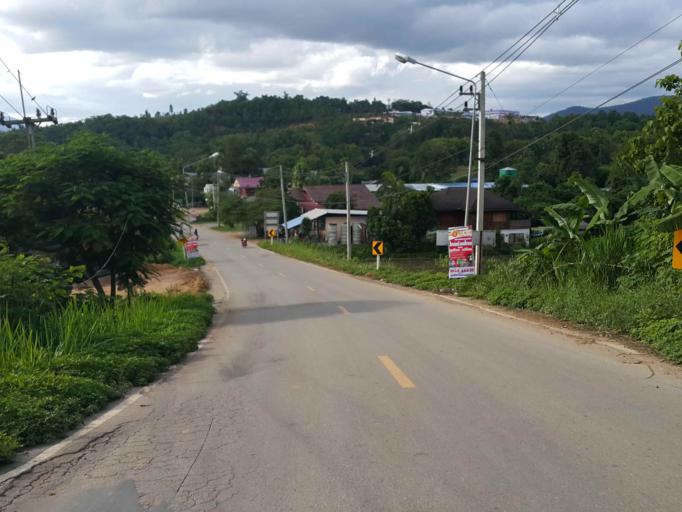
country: TH
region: Chiang Mai
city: Mae Chaem
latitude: 18.4894
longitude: 98.3776
